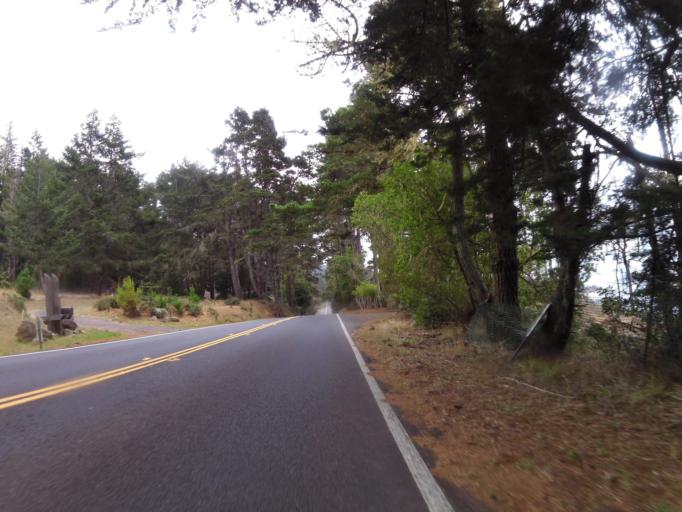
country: US
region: California
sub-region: Sonoma County
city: Sea Ranch
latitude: 38.5420
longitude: -123.2885
